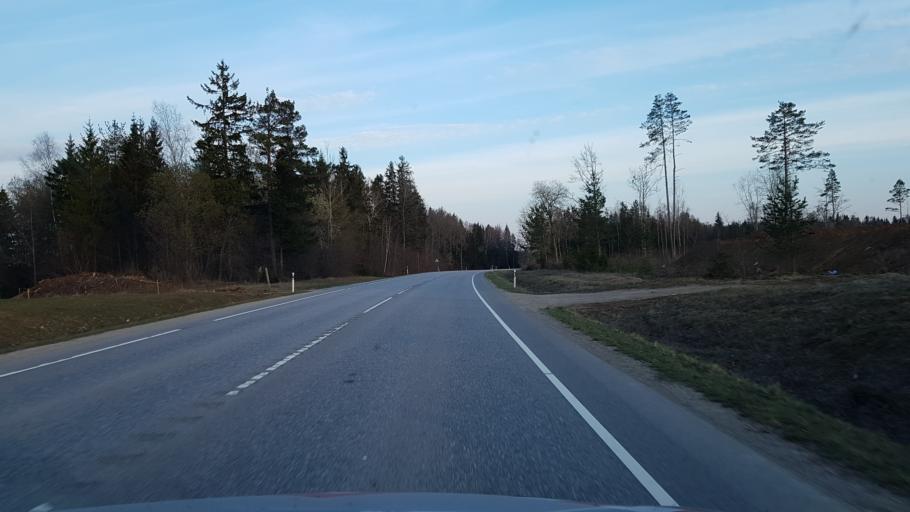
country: EE
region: Laeaene-Virumaa
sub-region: Someru vald
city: Someru
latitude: 59.3445
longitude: 26.4091
